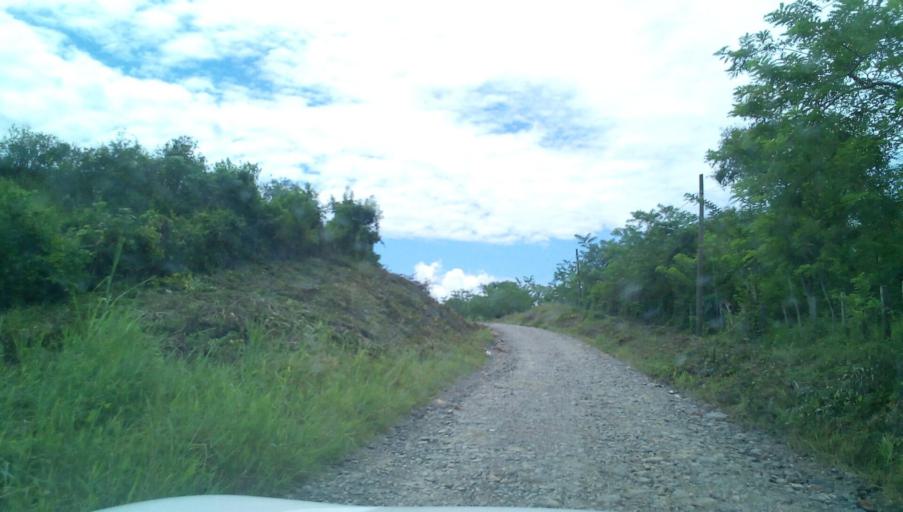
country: MX
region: Veracruz
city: Tepetzintla
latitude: 21.1534
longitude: -97.8543
